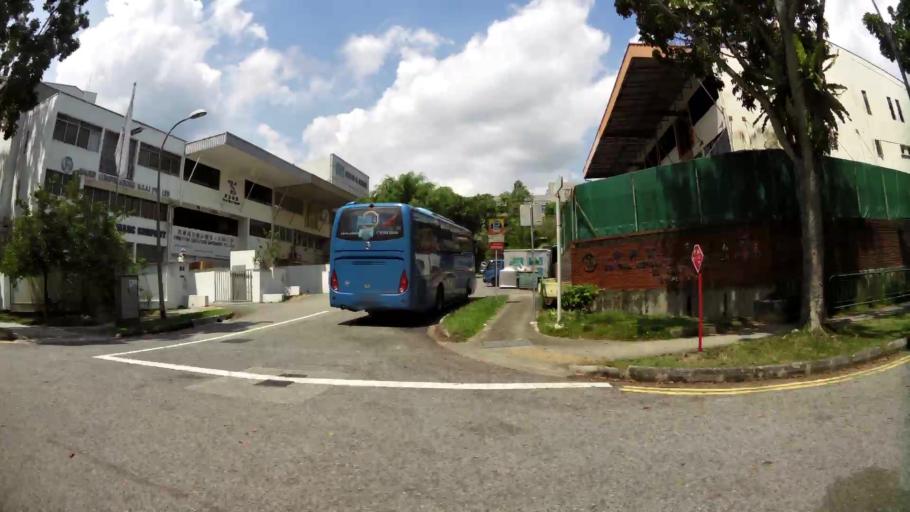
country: SG
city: Singapore
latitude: 1.3840
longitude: 103.8292
